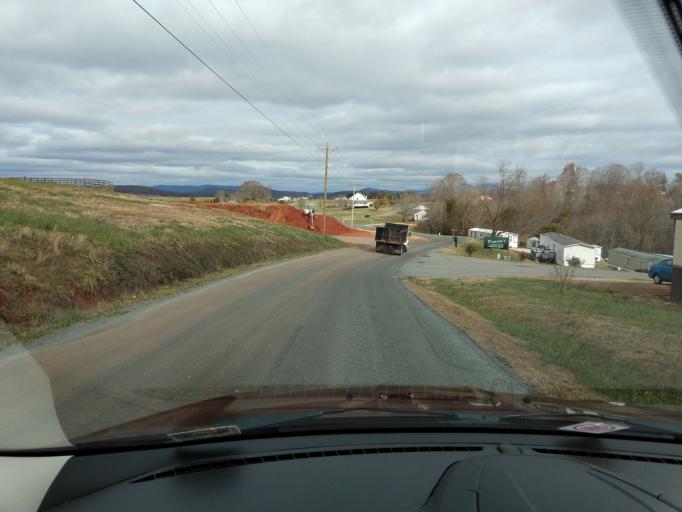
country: US
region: Virginia
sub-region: Franklin County
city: North Shore
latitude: 37.2014
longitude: -79.6860
